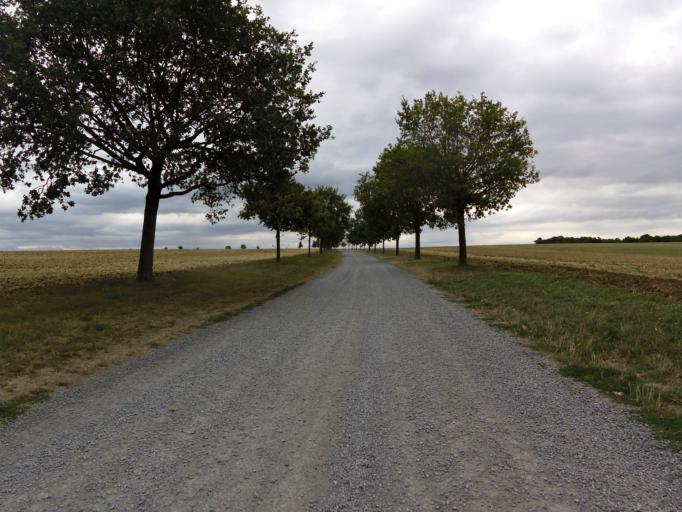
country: DE
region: Bavaria
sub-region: Regierungsbezirk Unterfranken
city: Wuerzburg
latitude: 49.8172
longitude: 9.9395
